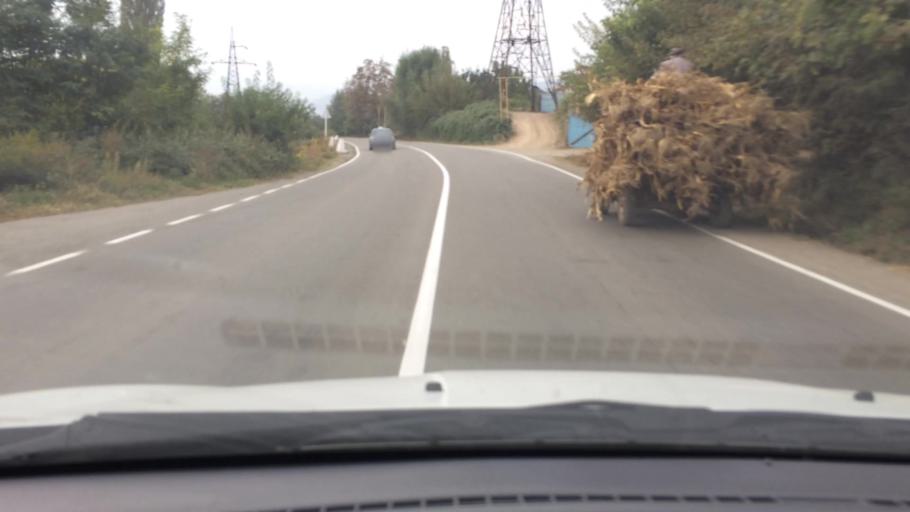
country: GE
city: Naghvarevi
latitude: 41.3258
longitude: 44.8006
